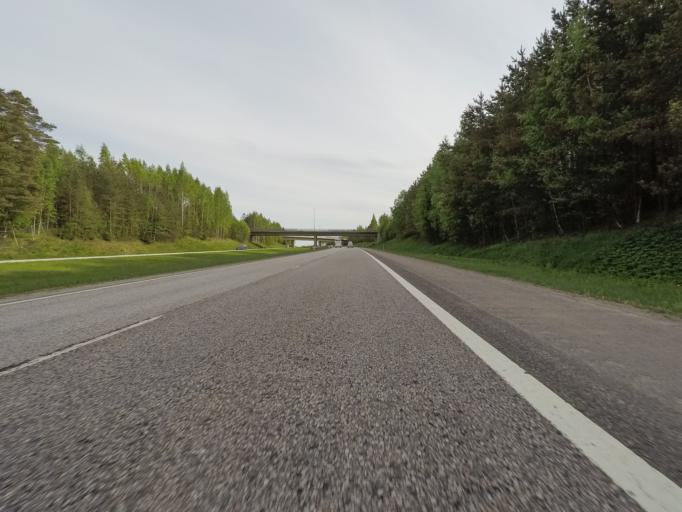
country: FI
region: Uusimaa
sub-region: Helsinki
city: Hyvinge
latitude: 60.5915
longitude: 24.7972
